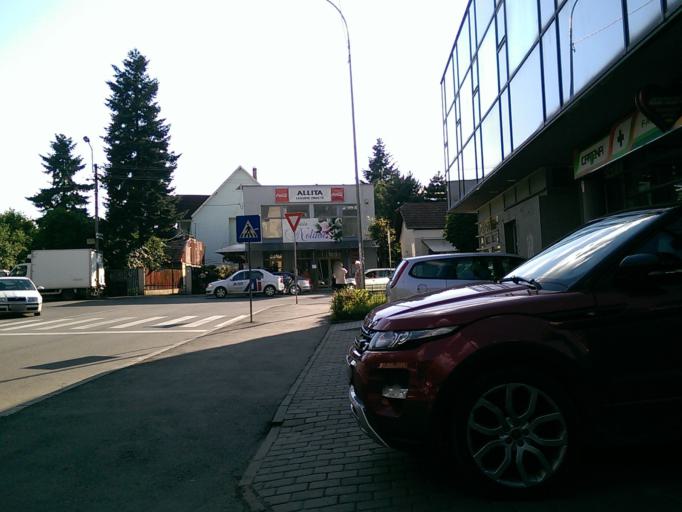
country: RO
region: Cluj
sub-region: Municipiul Cluj-Napoca
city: Cluj-Napoca
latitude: 46.7628
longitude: 23.6139
